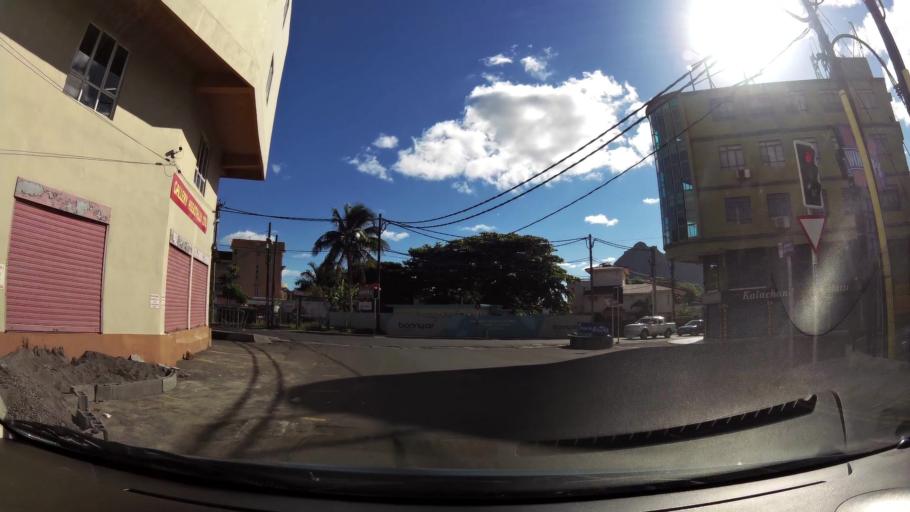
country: MU
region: Plaines Wilhems
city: Quatre Bornes
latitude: -20.2759
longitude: 57.4770
